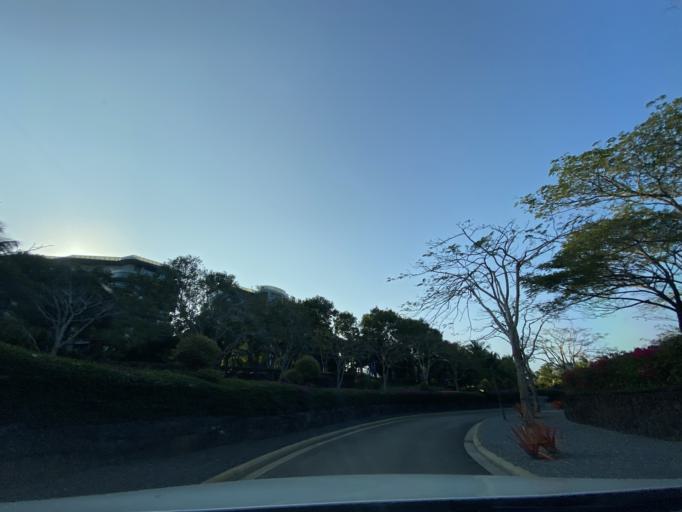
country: CN
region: Hainan
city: Xincun
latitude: 18.4185
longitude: 109.9506
